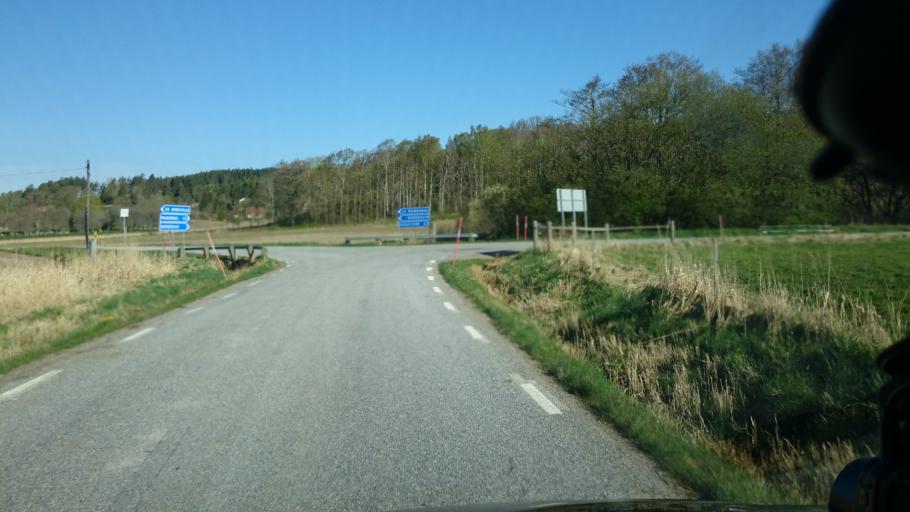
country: SE
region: Vaestra Goetaland
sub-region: Munkedals Kommun
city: Munkedal
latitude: 58.3778
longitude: 11.6778
